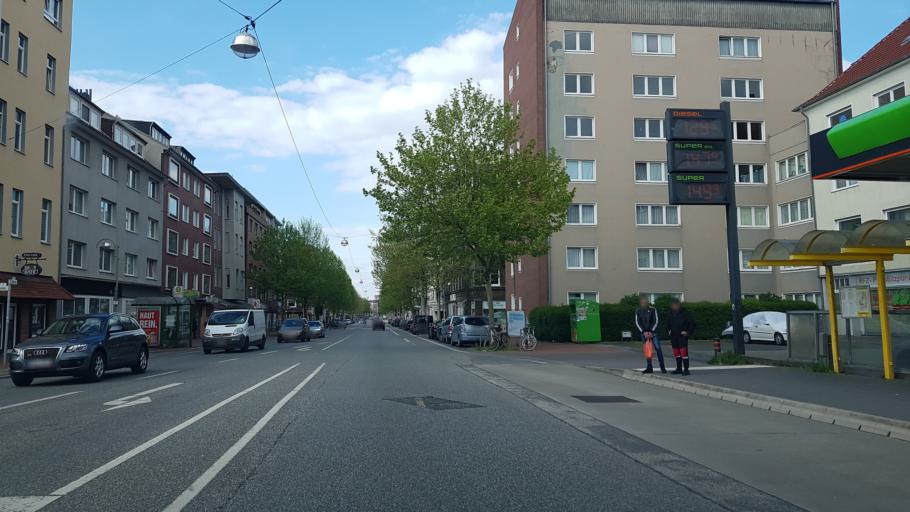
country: DE
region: Bremen
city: Bremerhaven
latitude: 53.5513
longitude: 8.5808
